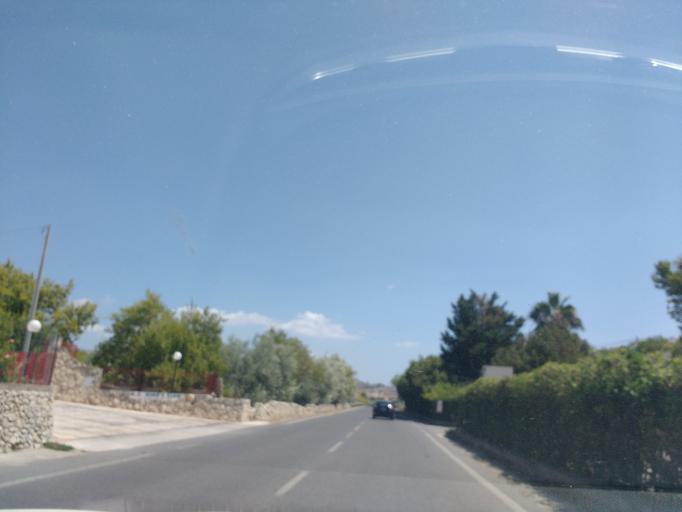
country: IT
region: Sicily
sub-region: Provincia di Siracusa
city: Noto
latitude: 36.8783
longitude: 15.0564
